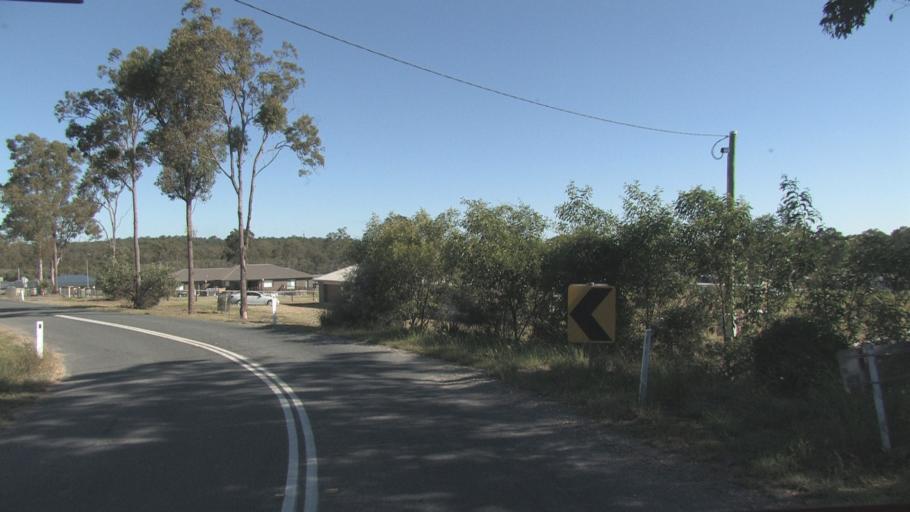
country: AU
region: Queensland
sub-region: Logan
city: Logan Reserve
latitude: -27.7518
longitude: 153.1413
